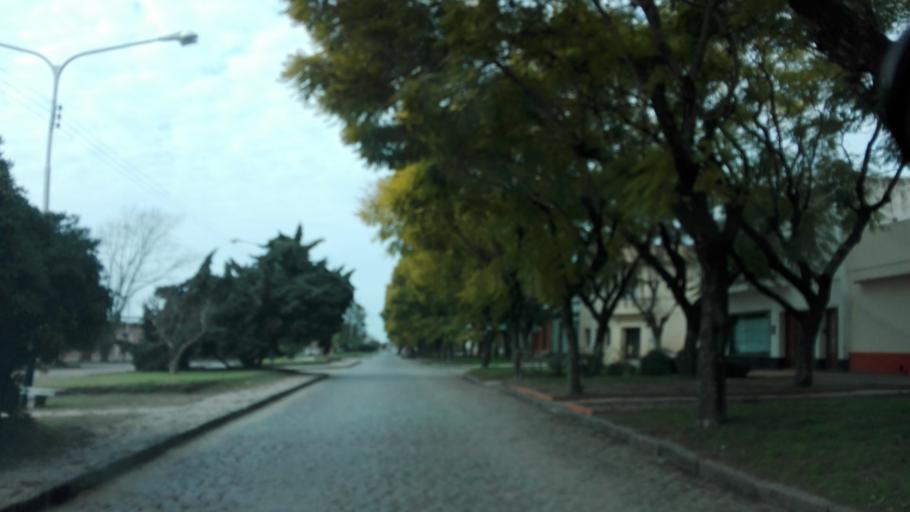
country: AR
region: Buenos Aires
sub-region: Partido de Chascomus
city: Chascomus
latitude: -35.5776
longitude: -58.0124
